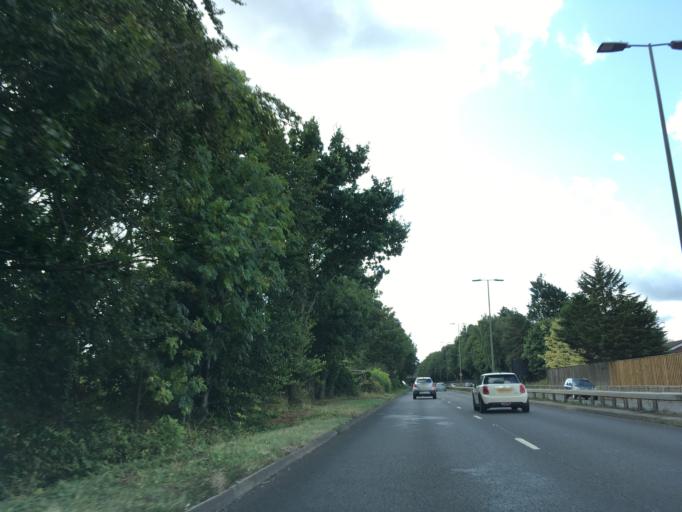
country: GB
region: England
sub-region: West Berkshire
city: Greenham
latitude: 51.3920
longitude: -1.3196
